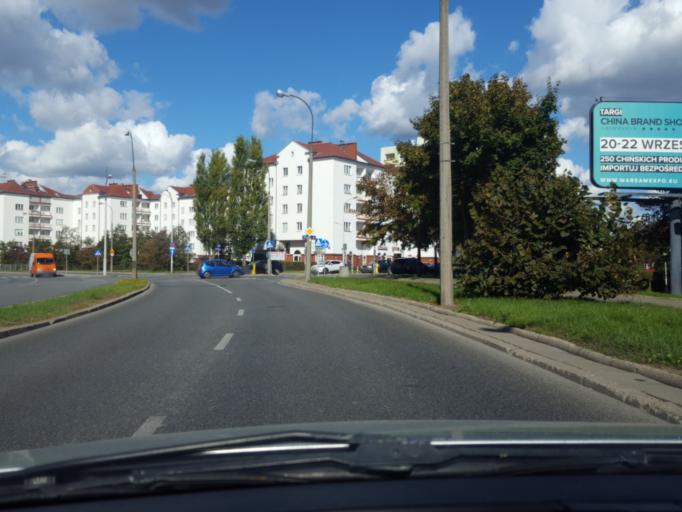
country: PL
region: Masovian Voivodeship
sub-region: Warszawa
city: Praga Poludnie
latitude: 52.2244
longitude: 21.1023
